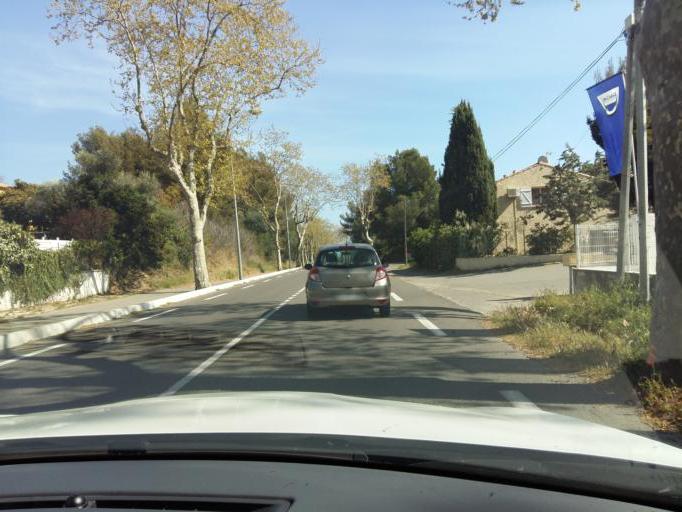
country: FR
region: Provence-Alpes-Cote d'Azur
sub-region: Departement du Var
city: Ollioules
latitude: 43.1339
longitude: 5.8611
